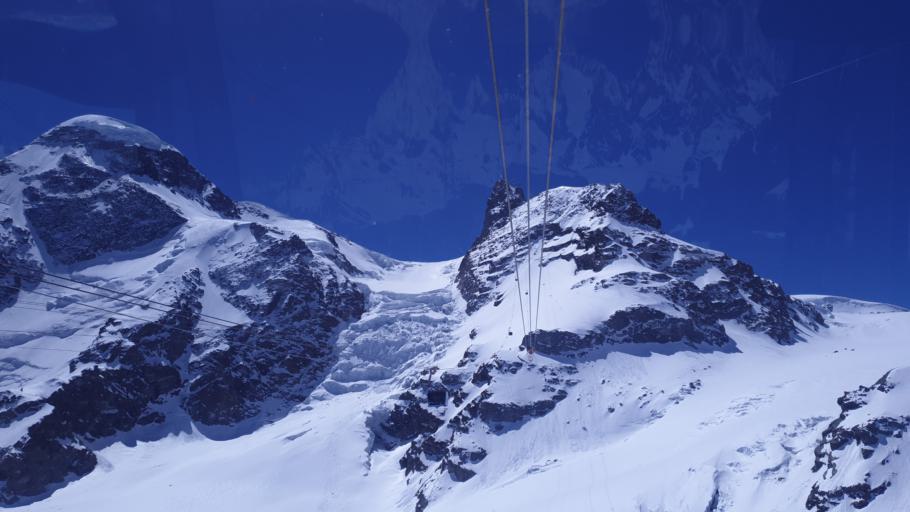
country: CH
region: Valais
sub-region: Visp District
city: Zermatt
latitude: 45.9573
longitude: 7.7247
